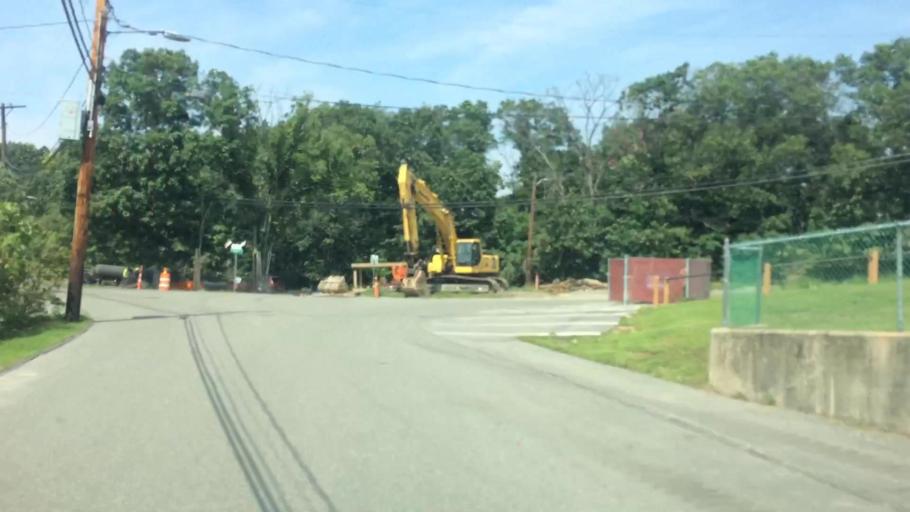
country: US
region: Massachusetts
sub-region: Norfolk County
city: Dedham
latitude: 42.2479
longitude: -71.1506
